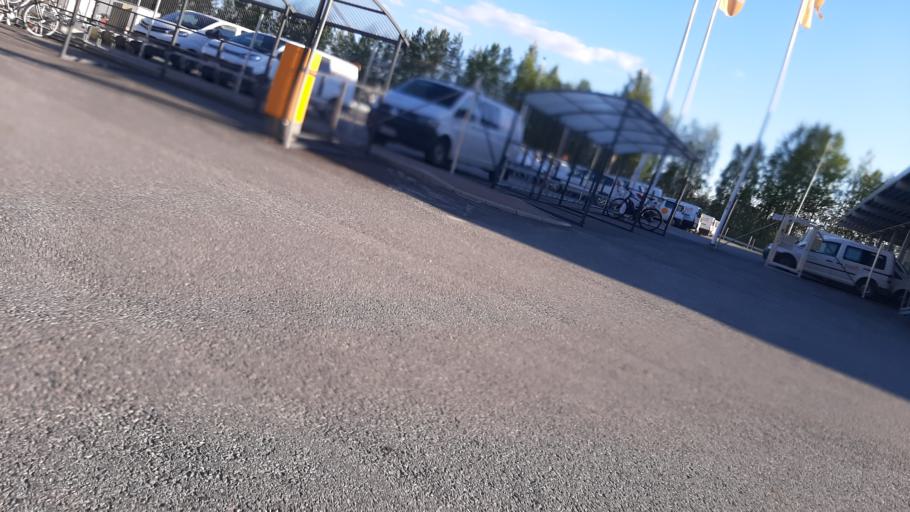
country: FI
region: North Karelia
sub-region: Joensuu
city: Joensuu
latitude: 62.6233
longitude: 29.7700
